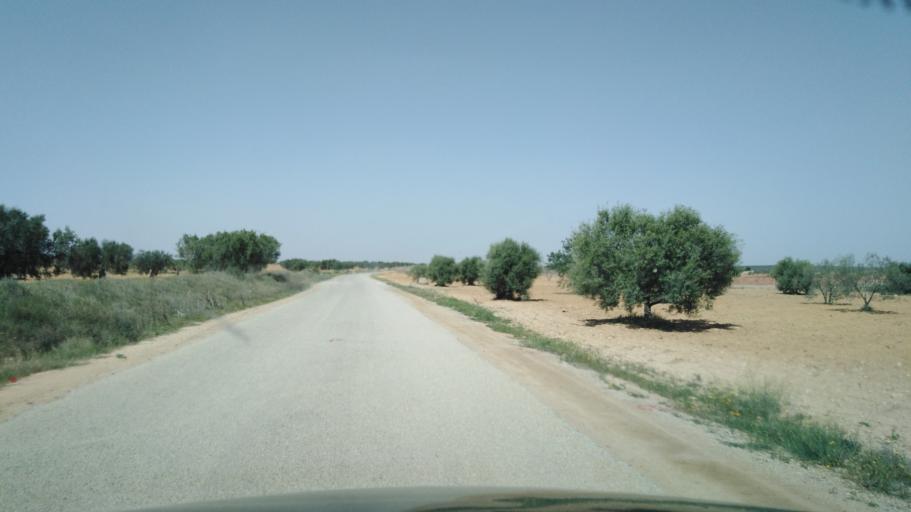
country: TN
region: Safaqis
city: Sfax
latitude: 34.6756
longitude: 10.4466
